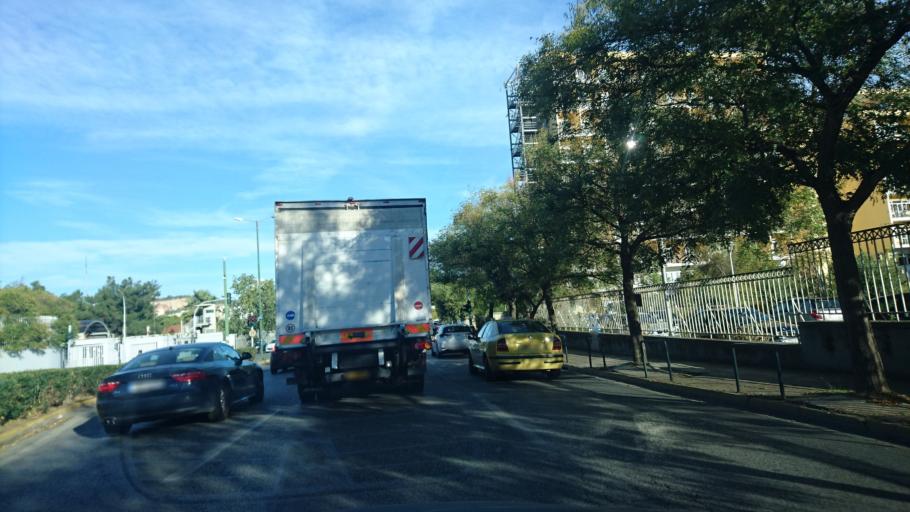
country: GR
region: Attica
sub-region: Nomarchia Athinas
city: Papagou
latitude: 37.9904
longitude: 23.7777
